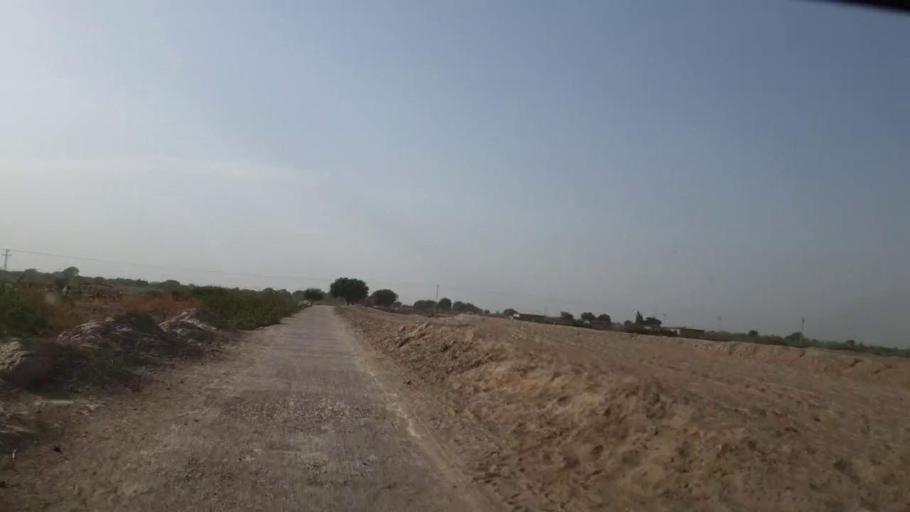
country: PK
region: Sindh
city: Naukot
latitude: 24.9807
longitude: 69.4935
